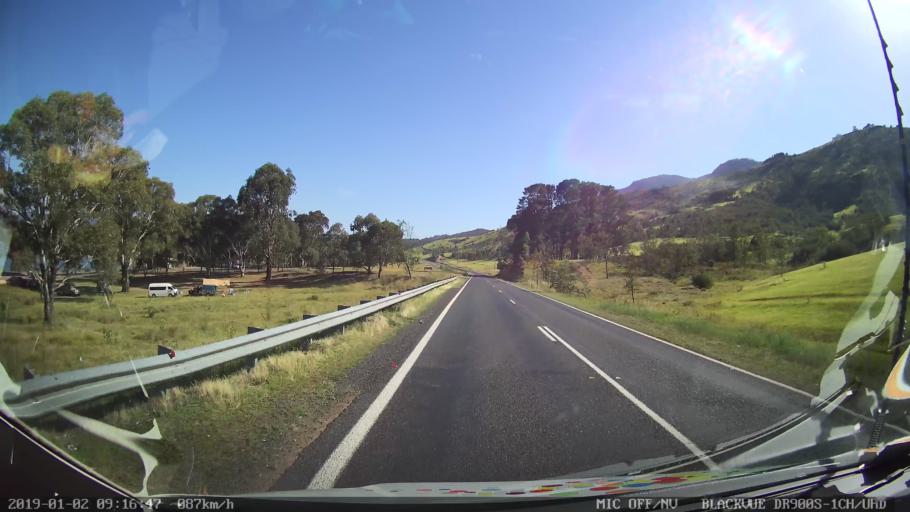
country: AU
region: New South Wales
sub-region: Tumut Shire
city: Tumut
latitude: -35.4493
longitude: 148.2851
